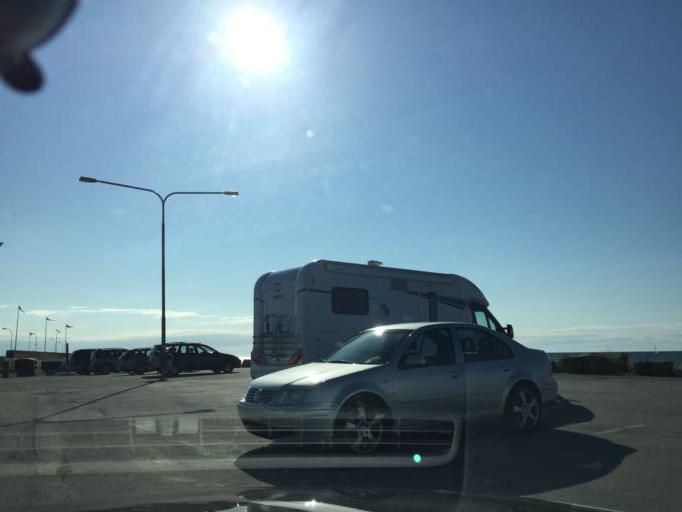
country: SE
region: Gotland
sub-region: Gotland
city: Visby
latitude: 57.6399
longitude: 18.2859
